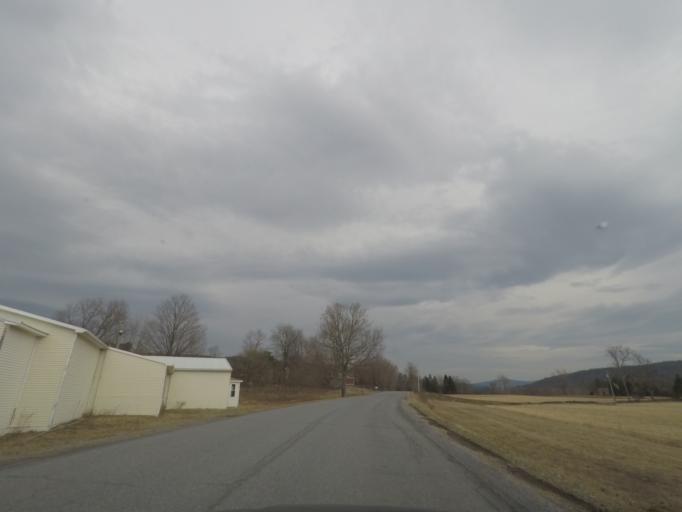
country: US
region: New York
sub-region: Rensselaer County
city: Hoosick Falls
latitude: 42.9499
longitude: -73.3766
